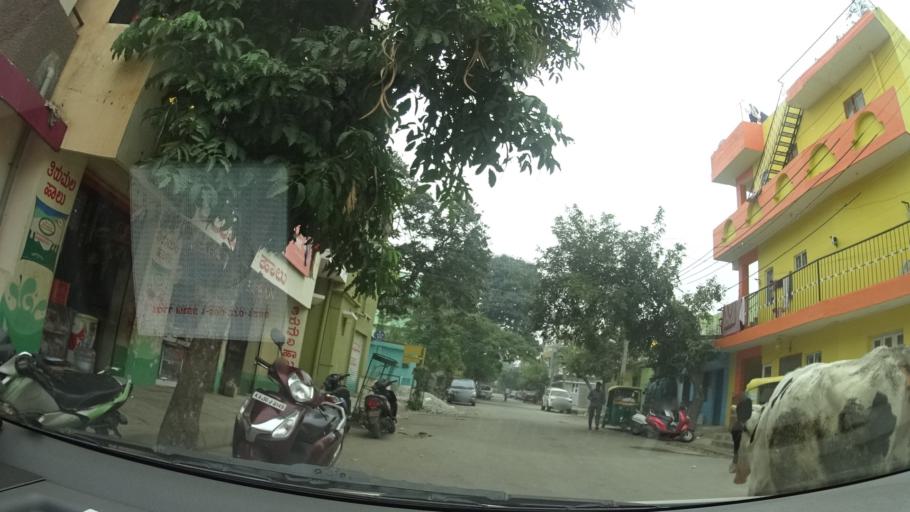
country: IN
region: Karnataka
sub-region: Bangalore Urban
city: Bangalore
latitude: 13.0349
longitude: 77.6310
